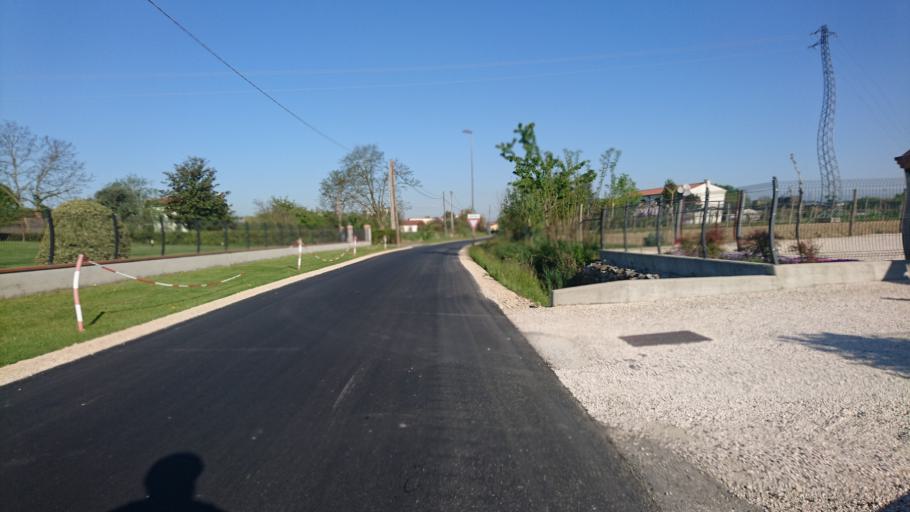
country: IT
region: Veneto
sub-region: Provincia di Padova
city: Massanzago-Ca' Baglioni-San Dono
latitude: 45.5459
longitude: 12.0014
